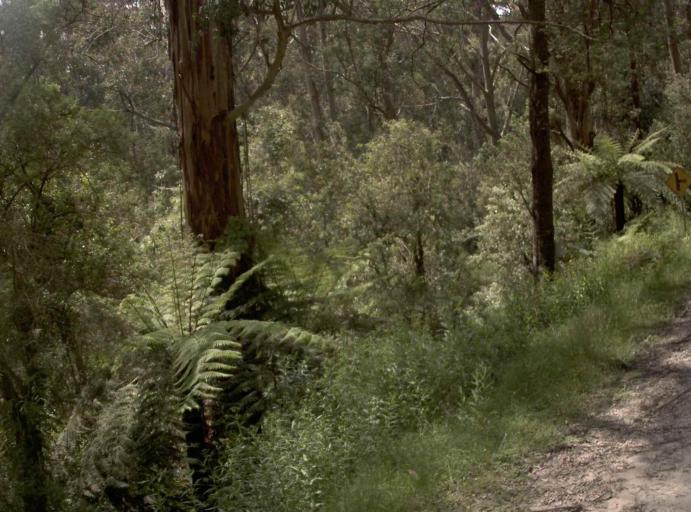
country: AU
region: Victoria
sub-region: Latrobe
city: Morwell
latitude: -38.4385
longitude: 146.5272
